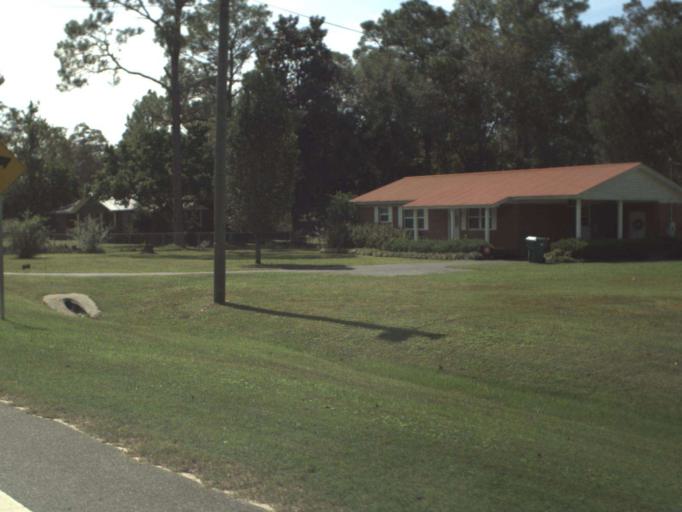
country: US
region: Florida
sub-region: Washington County
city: Chipley
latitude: 30.8035
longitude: -85.5340
